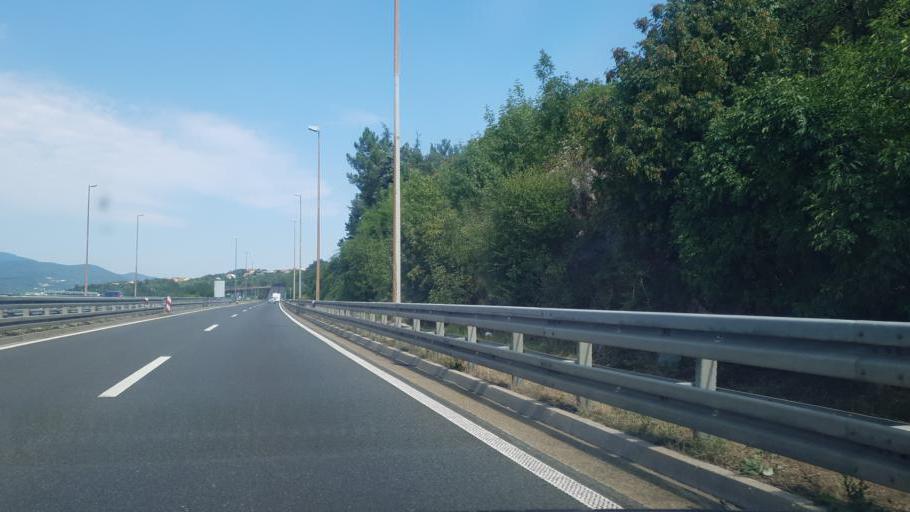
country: HR
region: Primorsko-Goranska
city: Rubesi
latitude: 45.3510
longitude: 14.3611
